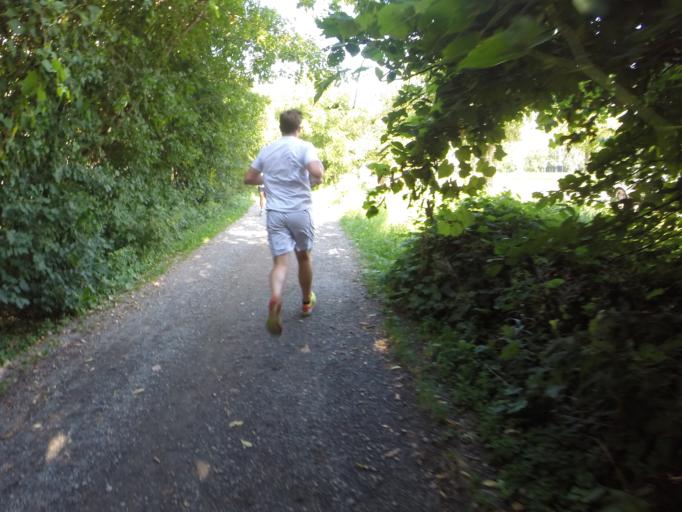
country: CA
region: Ontario
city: Toronto
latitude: 43.7039
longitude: -79.4212
